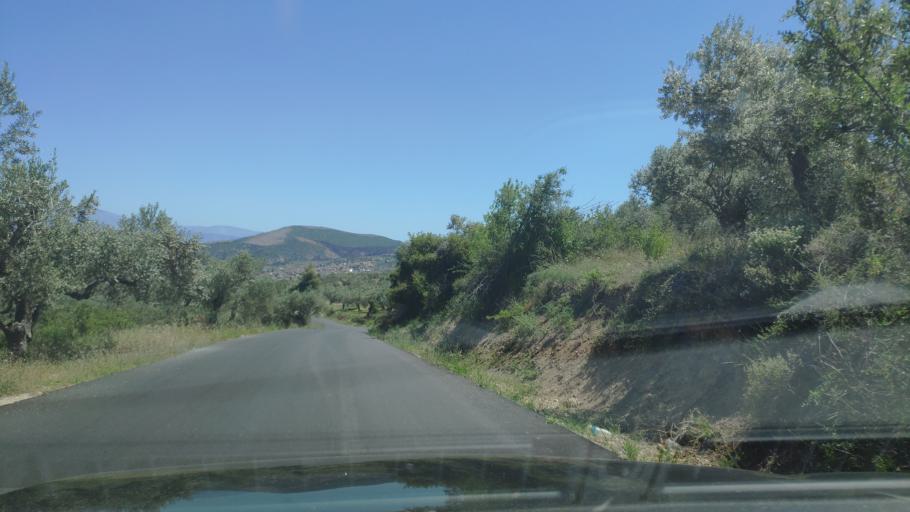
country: GR
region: Peloponnese
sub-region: Nomos Korinthias
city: Athikia
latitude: 37.8029
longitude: 22.9016
